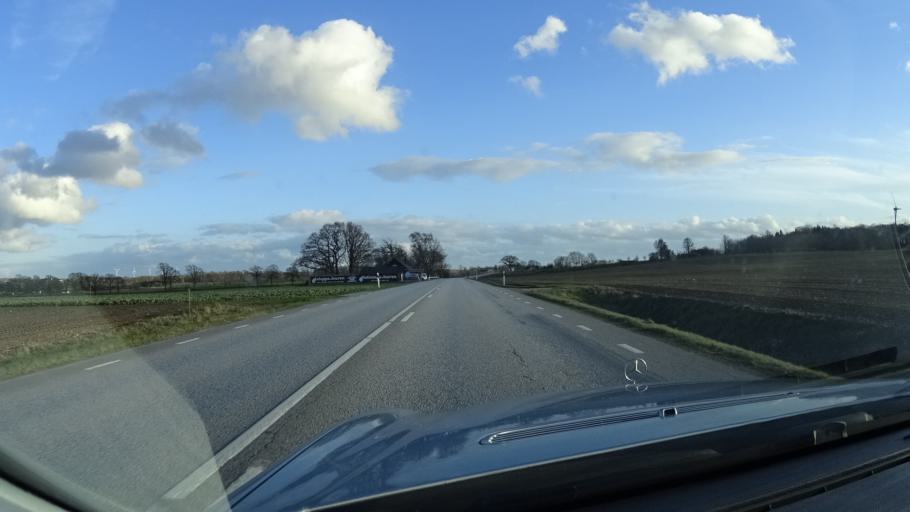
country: SE
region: Skane
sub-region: Hoors Kommun
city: Loberod
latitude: 55.8513
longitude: 13.4991
